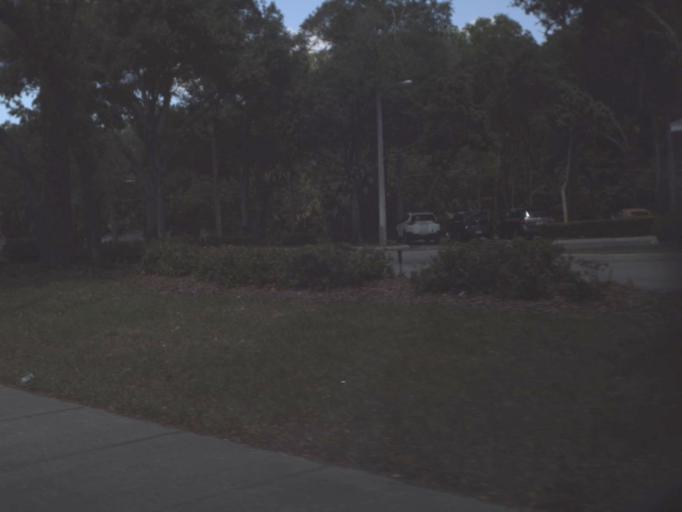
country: US
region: Florida
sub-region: Marion County
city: Ocala
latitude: 29.2035
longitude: -82.0778
